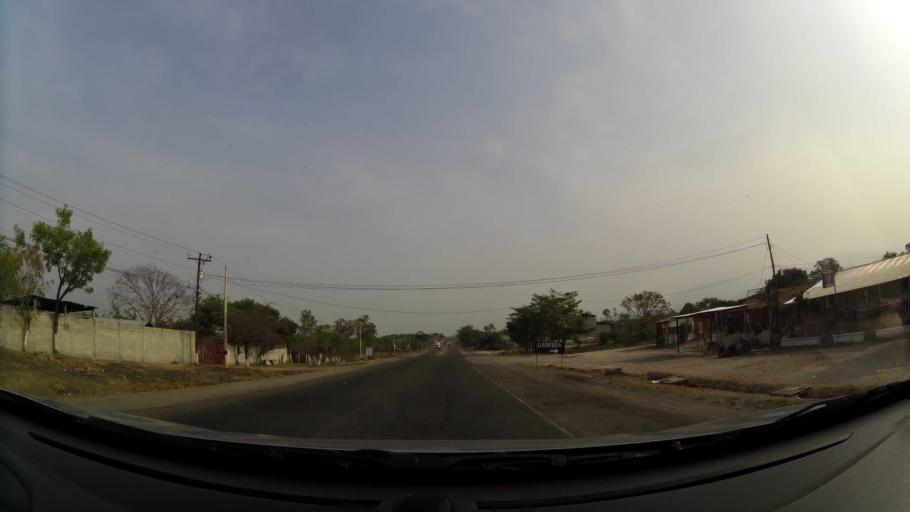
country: HN
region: Comayagua
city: Flores
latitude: 14.3112
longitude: -87.5799
